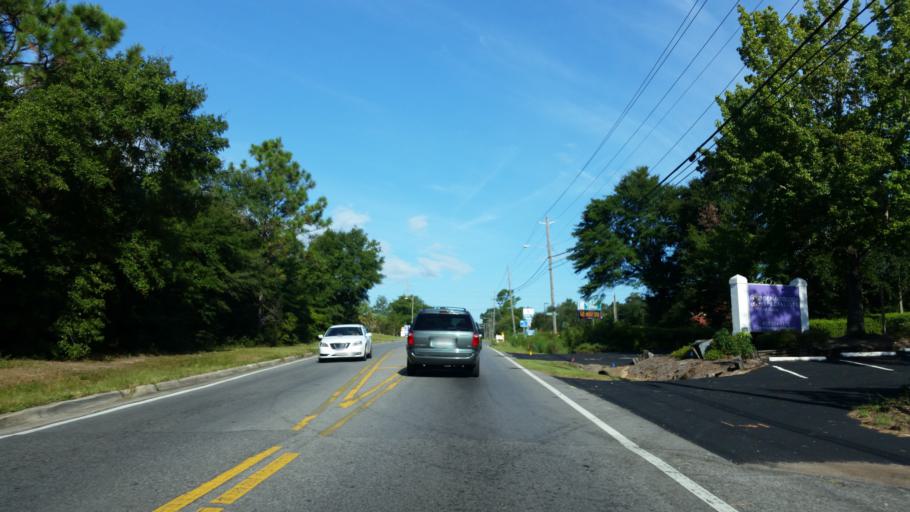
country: US
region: Florida
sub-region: Santa Rosa County
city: Milton
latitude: 30.6332
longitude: -87.0694
